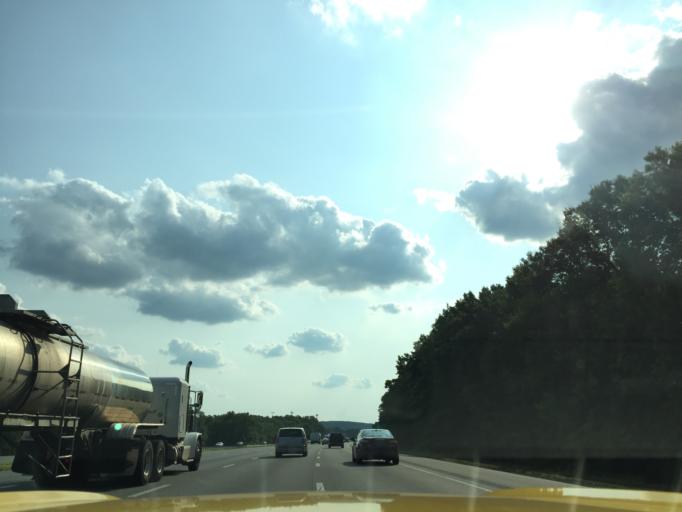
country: US
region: Delaware
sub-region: New Castle County
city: Brookside
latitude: 39.6549
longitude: -75.7041
